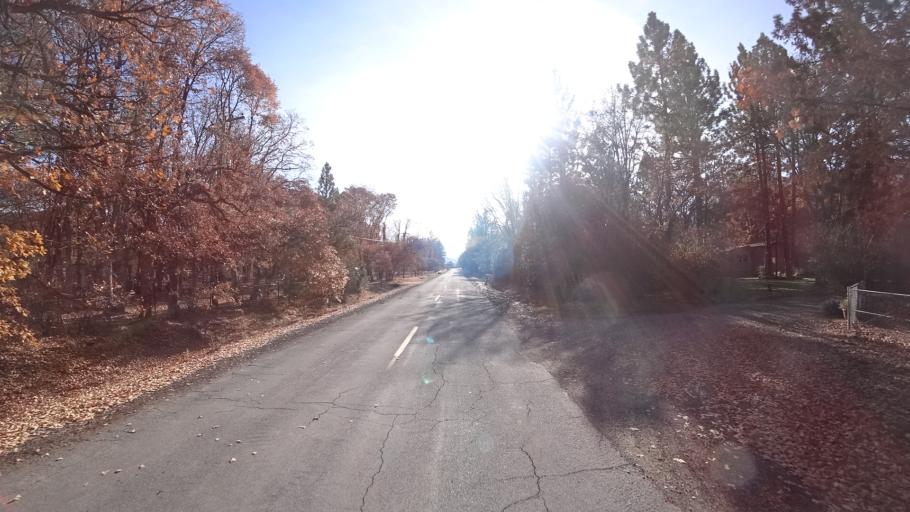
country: US
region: California
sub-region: Siskiyou County
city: Yreka
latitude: 41.6665
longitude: -122.6056
